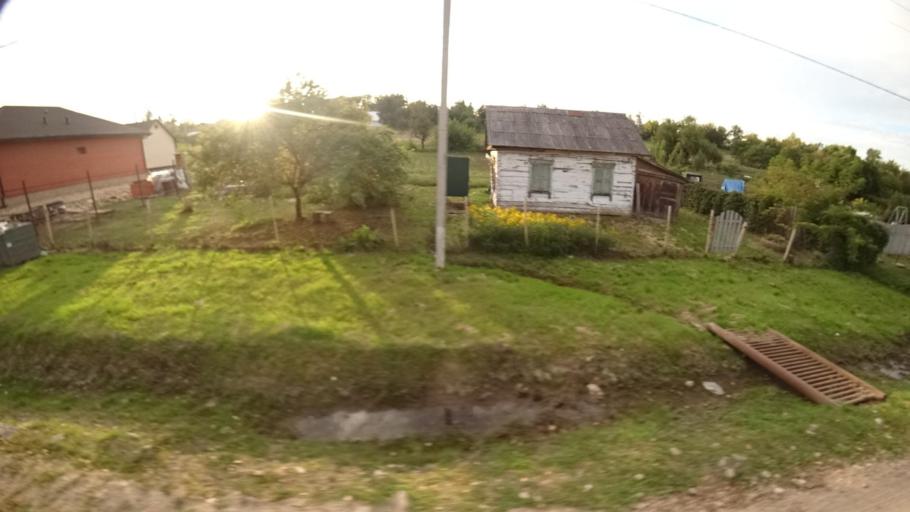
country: RU
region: Primorskiy
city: Yakovlevka
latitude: 44.4243
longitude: 133.4802
